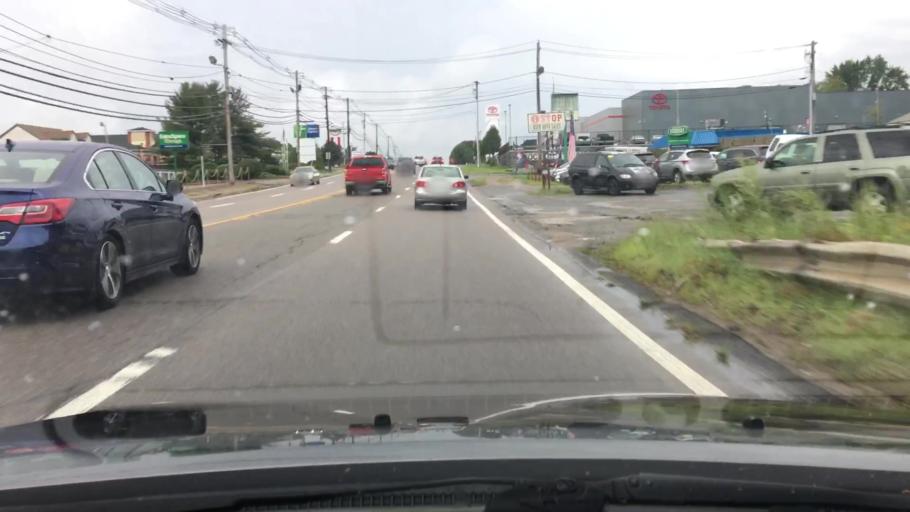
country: US
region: Massachusetts
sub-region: Norfolk County
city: Plainville
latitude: 41.9576
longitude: -71.3424
